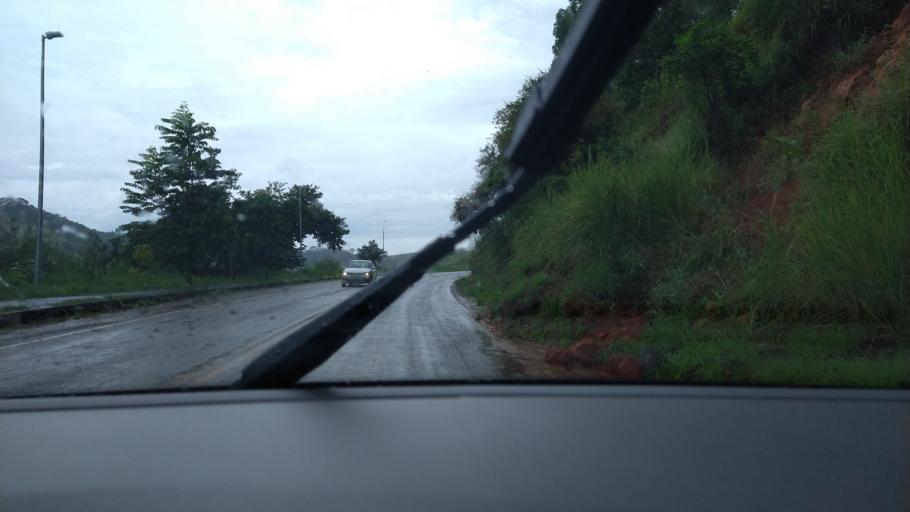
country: BR
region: Minas Gerais
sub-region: Ponte Nova
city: Ponte Nova
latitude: -20.3918
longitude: -42.9014
